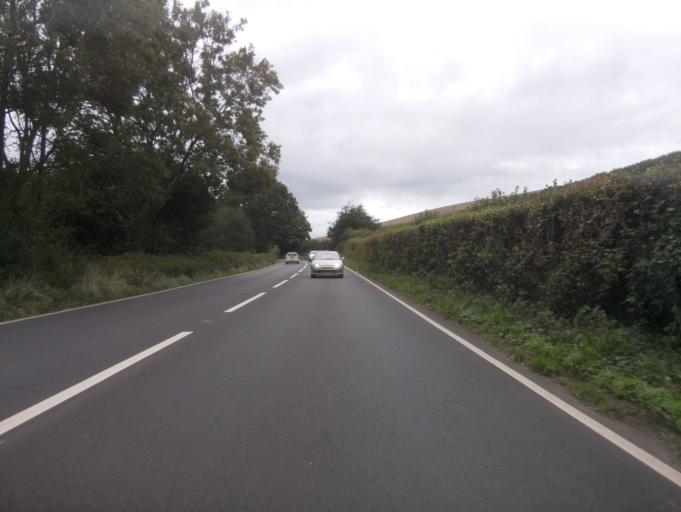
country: GB
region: England
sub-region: Devon
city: Totnes
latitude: 50.4296
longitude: -3.6488
